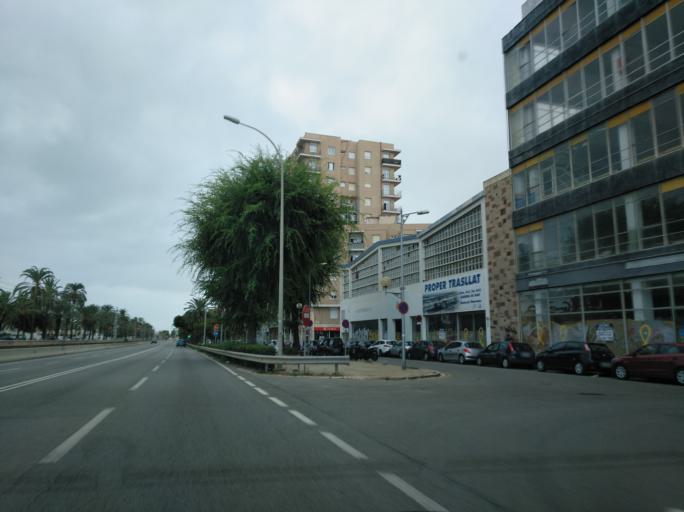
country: ES
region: Catalonia
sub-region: Provincia de Barcelona
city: Mataro
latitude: 41.5403
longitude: 2.4550
